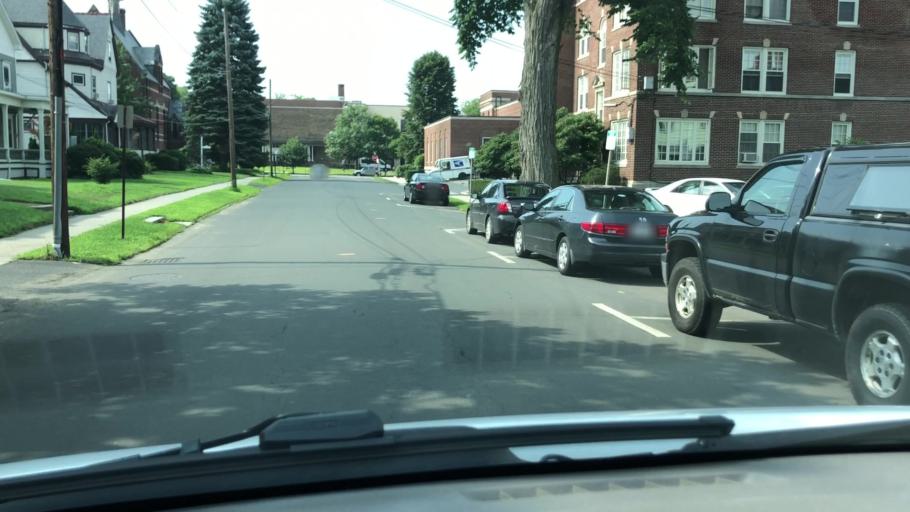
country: US
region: Massachusetts
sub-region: Franklin County
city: Greenfield
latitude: 42.5887
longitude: -72.5972
